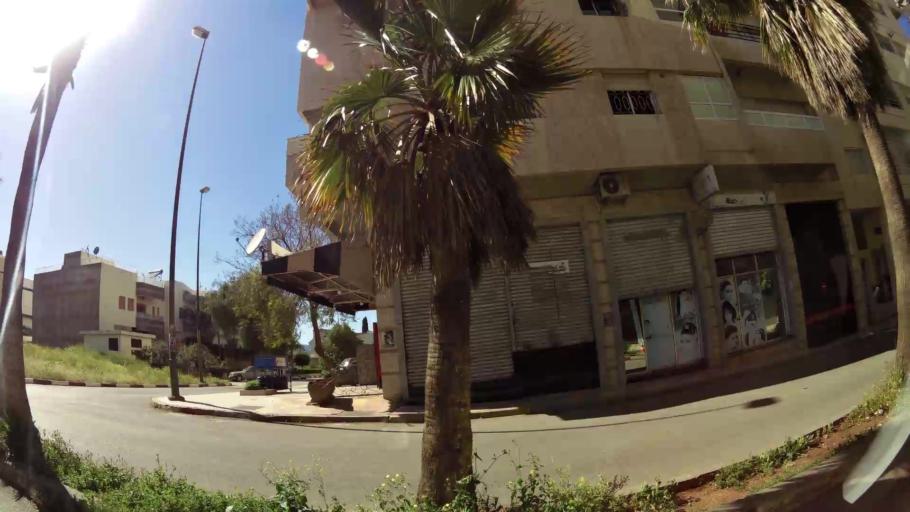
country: MA
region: Fes-Boulemane
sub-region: Fes
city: Fes
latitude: 34.0209
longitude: -4.9882
